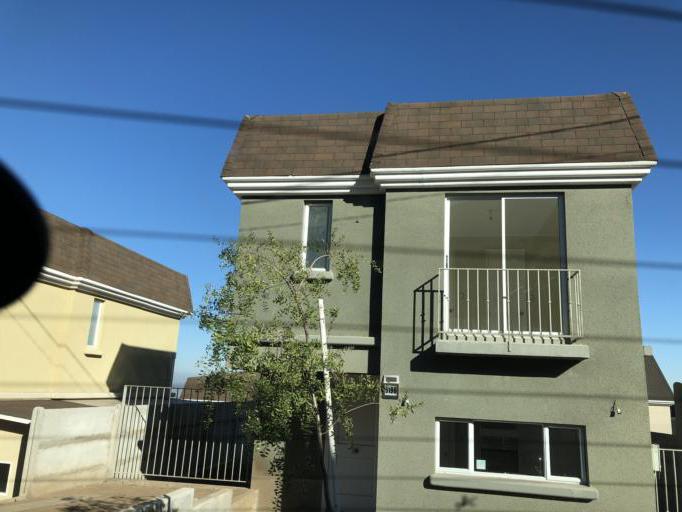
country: CL
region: Santiago Metropolitan
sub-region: Provincia de Cordillera
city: Puente Alto
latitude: -33.5530
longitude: -70.5318
